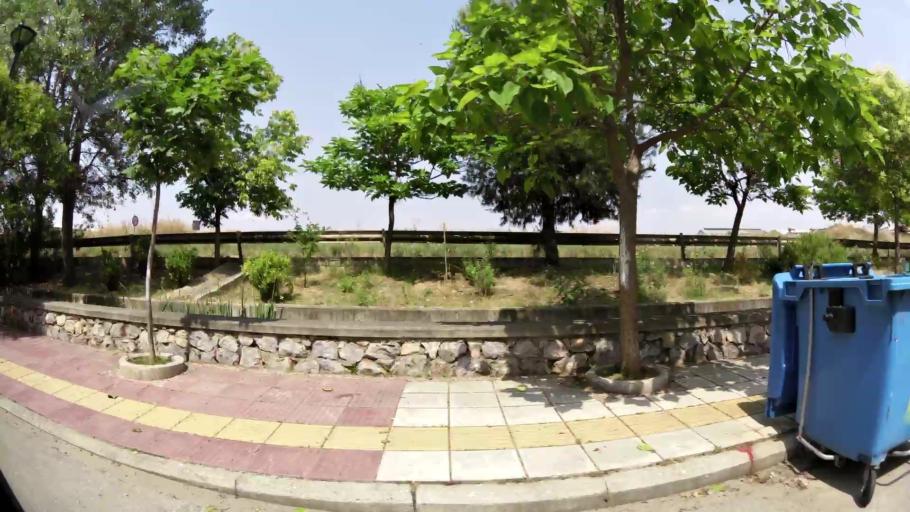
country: GR
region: Central Macedonia
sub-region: Nomos Thessalonikis
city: Diavata
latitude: 40.6886
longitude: 22.8618
